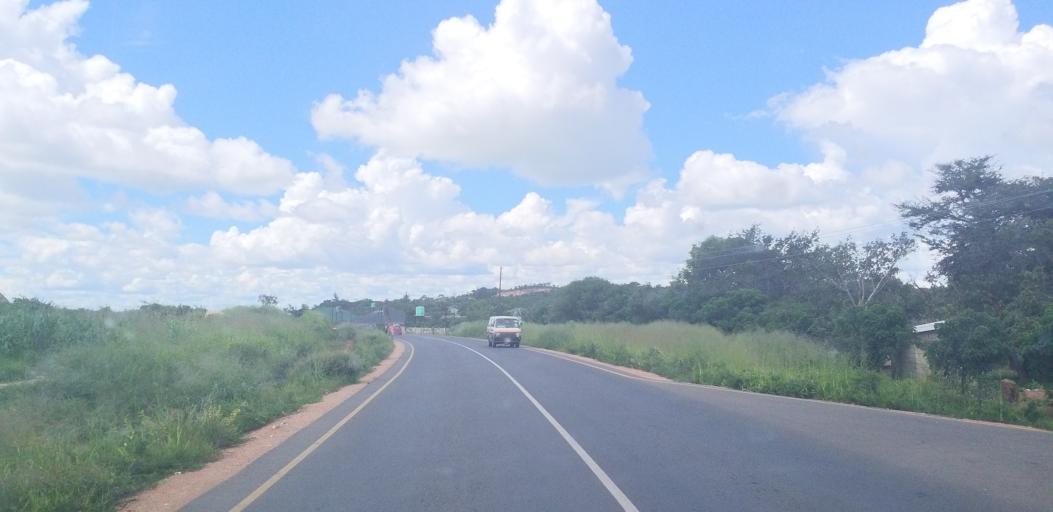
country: ZM
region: Lusaka
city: Lusaka
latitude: -15.3310
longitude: 28.3288
